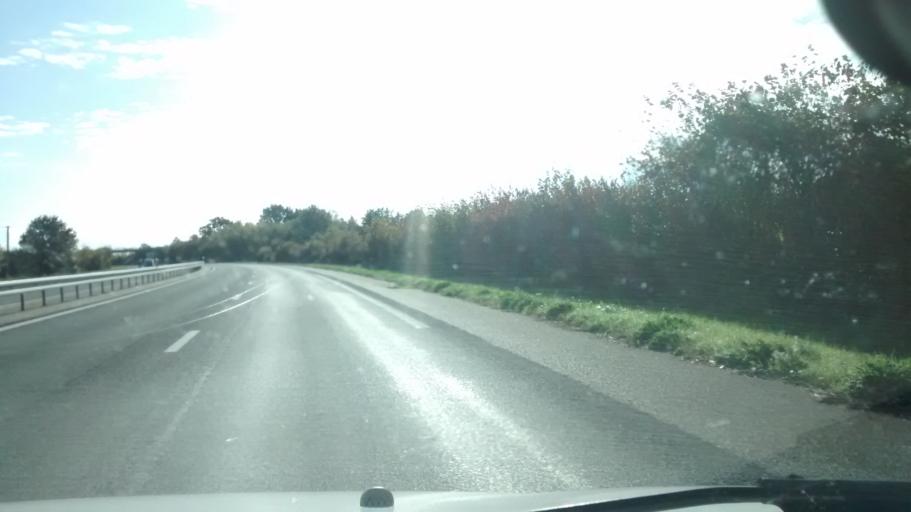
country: FR
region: Pays de la Loire
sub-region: Departement de Maine-et-Loire
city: Pouance
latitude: 47.7409
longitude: -1.1529
